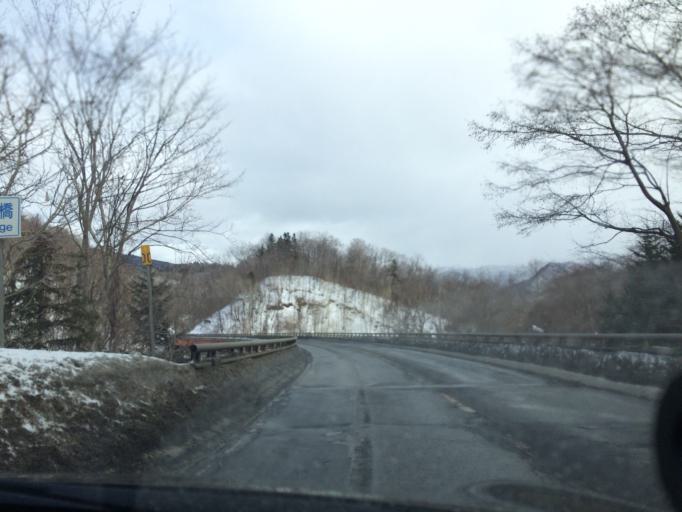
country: JP
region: Hokkaido
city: Shimo-furano
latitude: 42.8865
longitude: 142.2367
